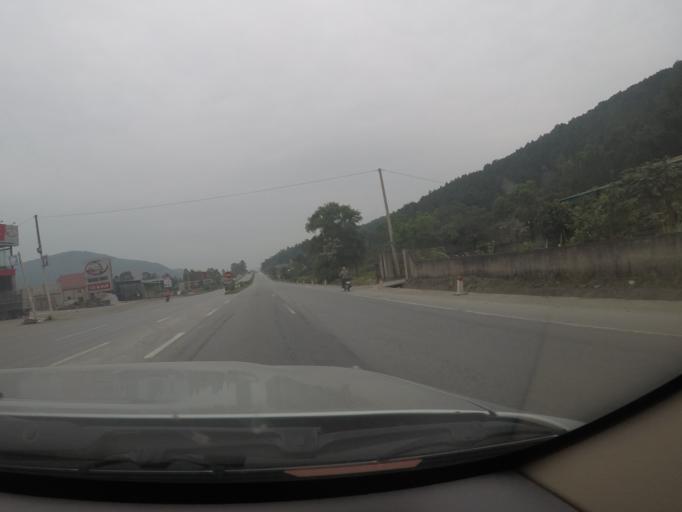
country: VN
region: Nghe An
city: Quan Hanh
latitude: 18.8640
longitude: 105.6355
